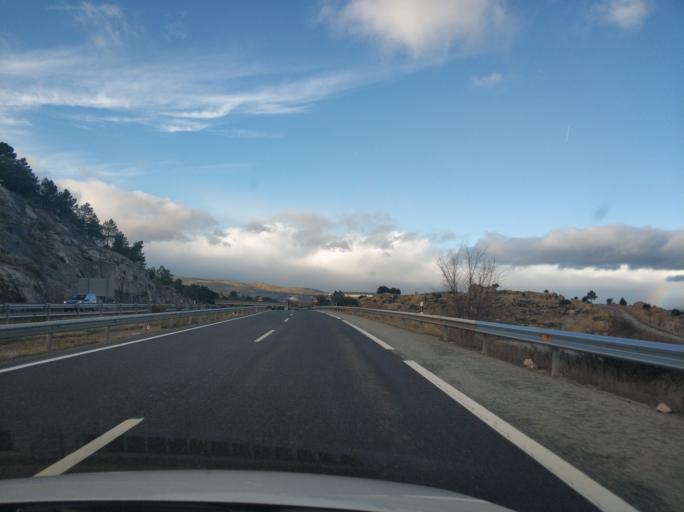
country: ES
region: Madrid
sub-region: Provincia de Madrid
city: La Cabrera
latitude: 40.8887
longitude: -3.5997
